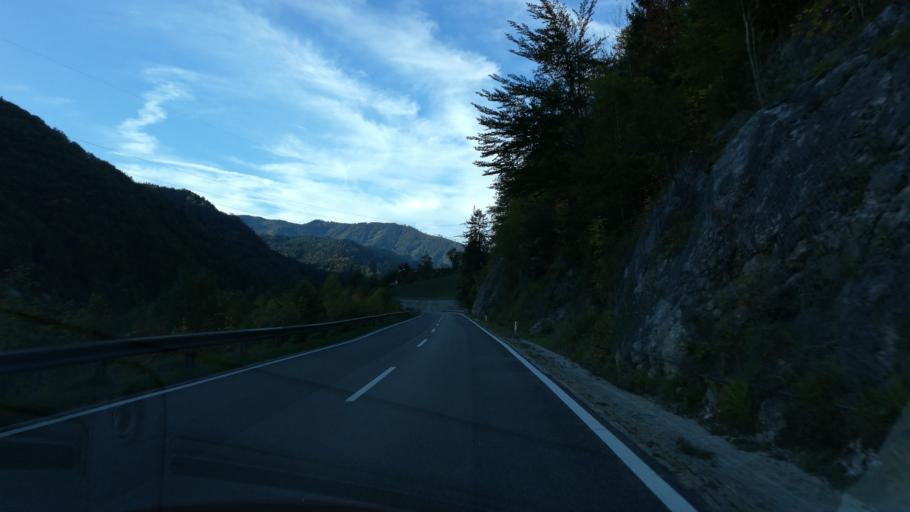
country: AT
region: Styria
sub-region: Politischer Bezirk Liezen
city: Altenmarkt bei Sankt Gallen
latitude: 47.7804
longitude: 14.6532
